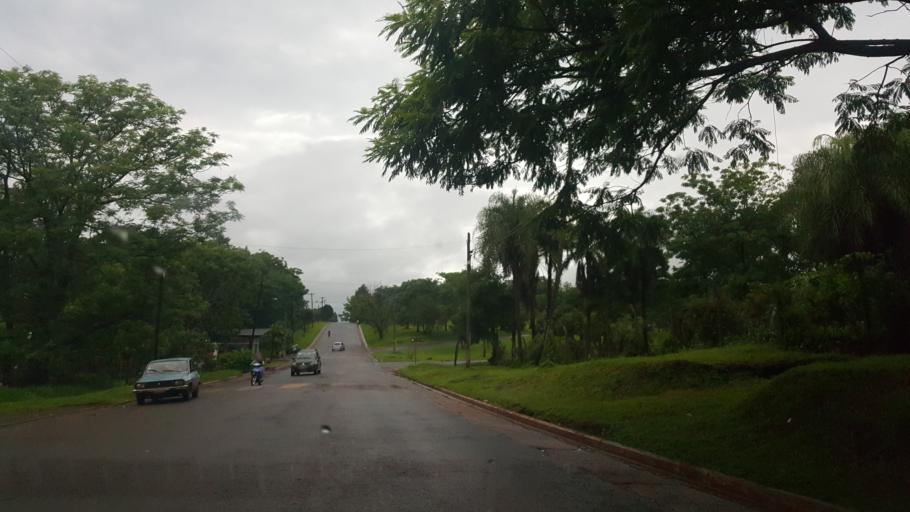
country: AR
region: Misiones
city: Santo Pipo
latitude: -27.1376
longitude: -55.4102
